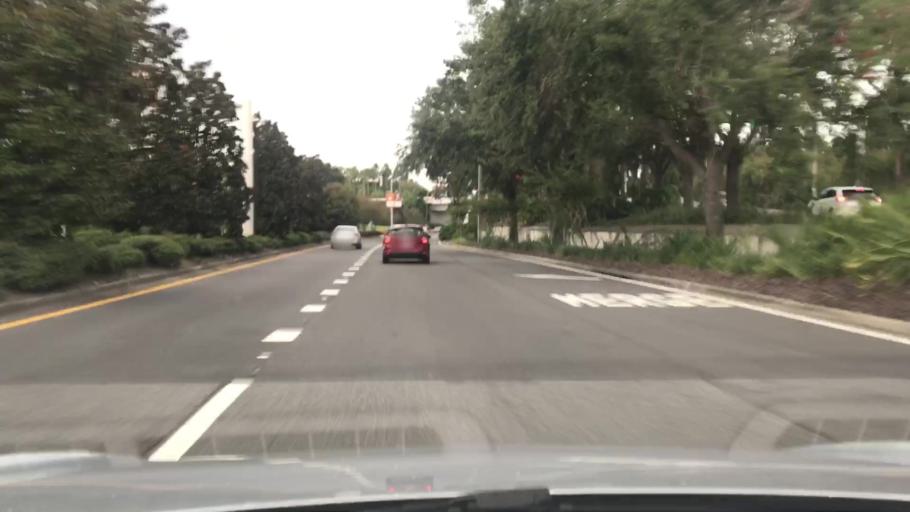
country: US
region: Florida
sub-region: Orange County
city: Belle Isle
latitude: 28.4364
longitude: -81.3071
